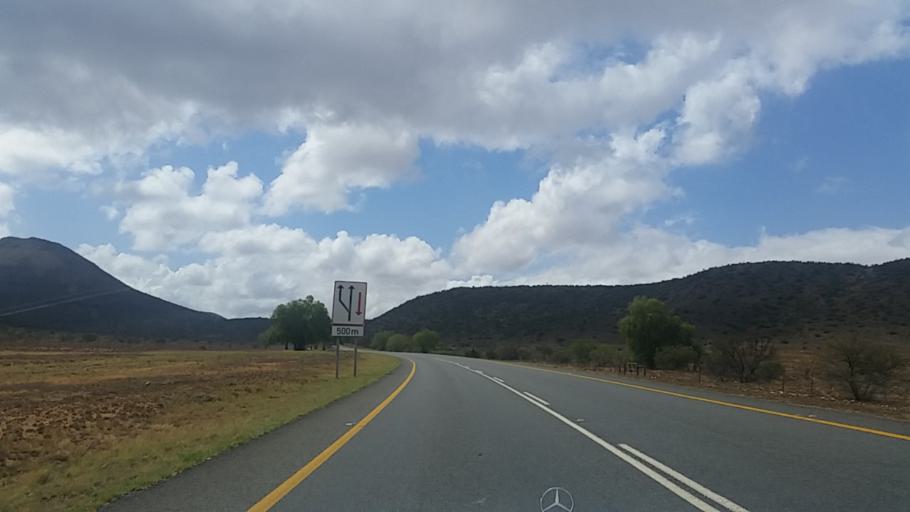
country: ZA
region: Eastern Cape
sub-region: Cacadu District Municipality
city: Graaff-Reinet
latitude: -32.0717
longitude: 24.6050
